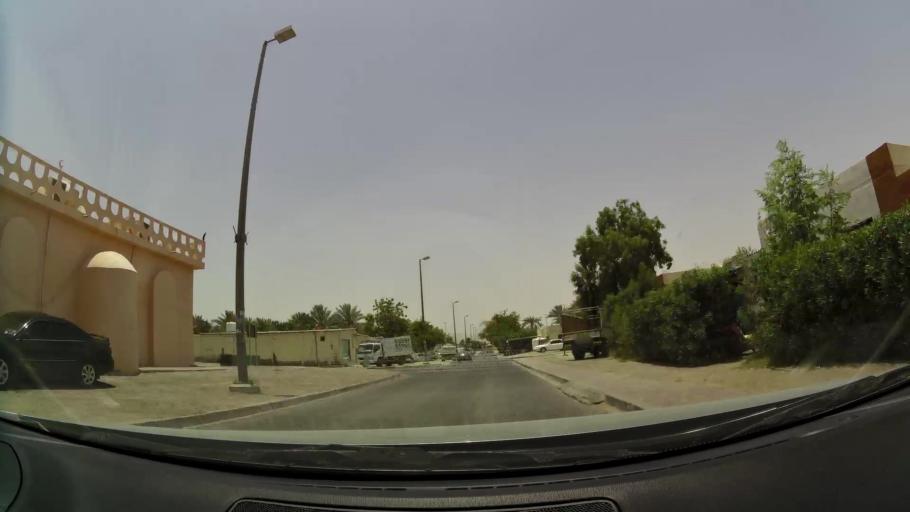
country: AE
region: Abu Dhabi
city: Al Ain
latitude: 24.2075
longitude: 55.7550
